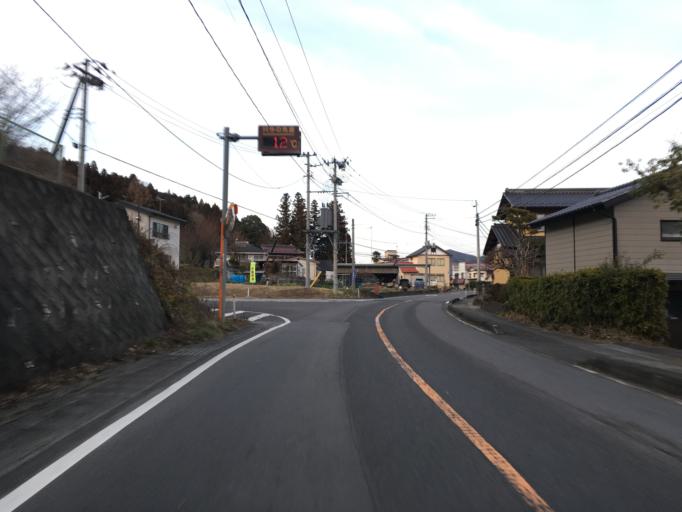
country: JP
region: Ibaraki
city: Daigo
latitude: 36.9040
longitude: 140.4063
